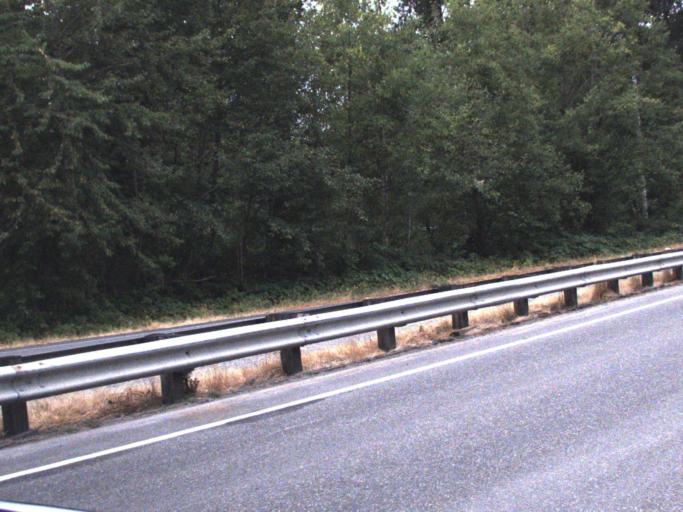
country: US
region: Washington
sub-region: King County
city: Fall City
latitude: 47.5614
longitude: -121.8615
